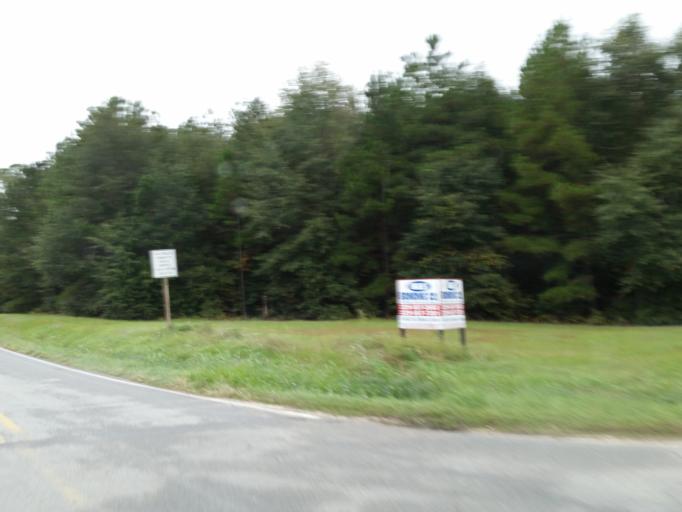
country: US
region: Georgia
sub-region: Turner County
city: Ashburn
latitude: 31.6854
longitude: -83.6401
